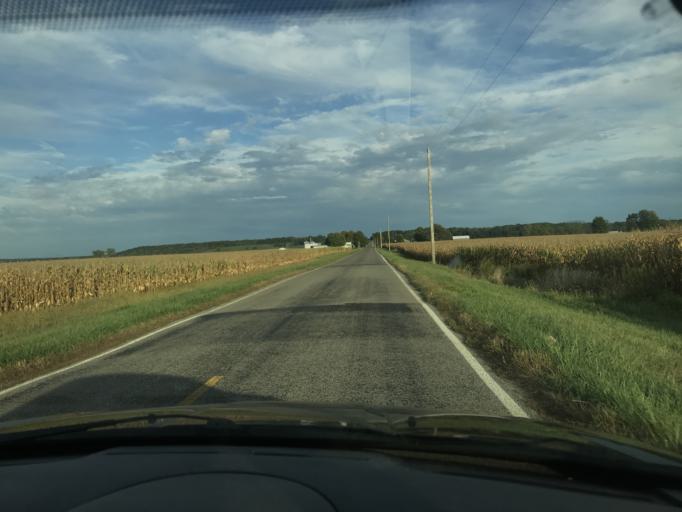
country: US
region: Ohio
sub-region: Logan County
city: West Liberty
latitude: 40.1945
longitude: -83.7936
